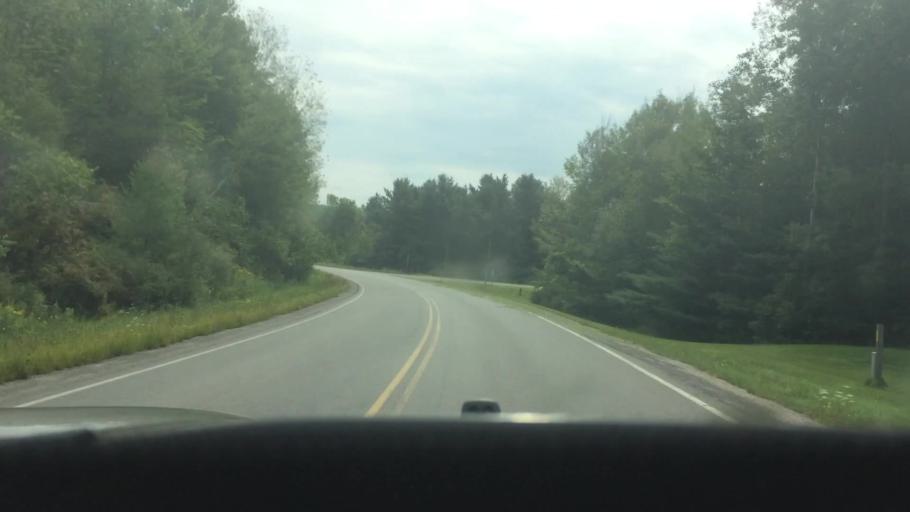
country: US
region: New York
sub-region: St. Lawrence County
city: Canton
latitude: 44.4962
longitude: -75.2624
